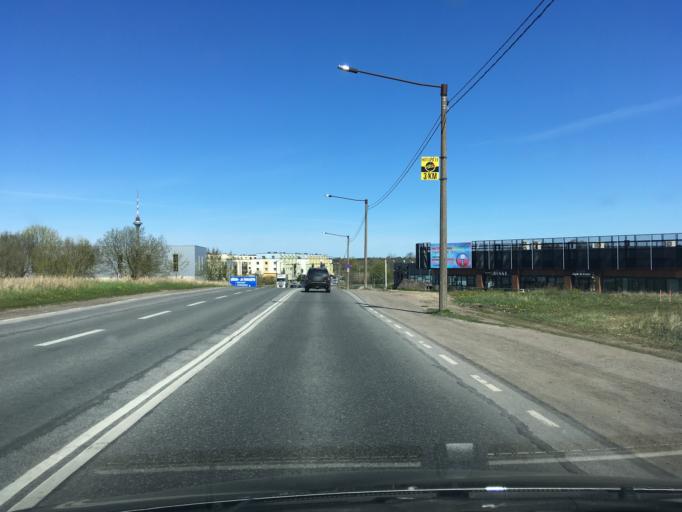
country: EE
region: Harju
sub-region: Tallinna linn
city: Kose
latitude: 59.4502
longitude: 24.8911
